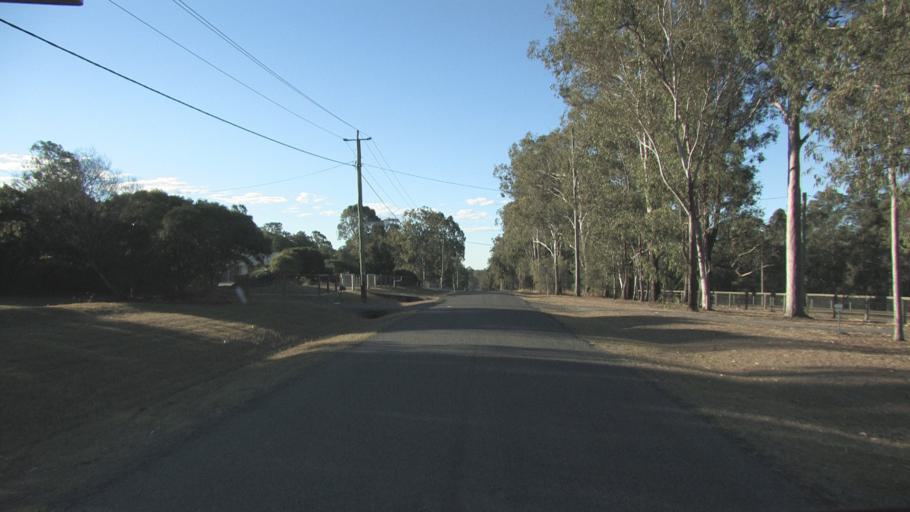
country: AU
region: Queensland
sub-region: Logan
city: Cedar Vale
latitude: -27.8703
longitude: 152.9754
